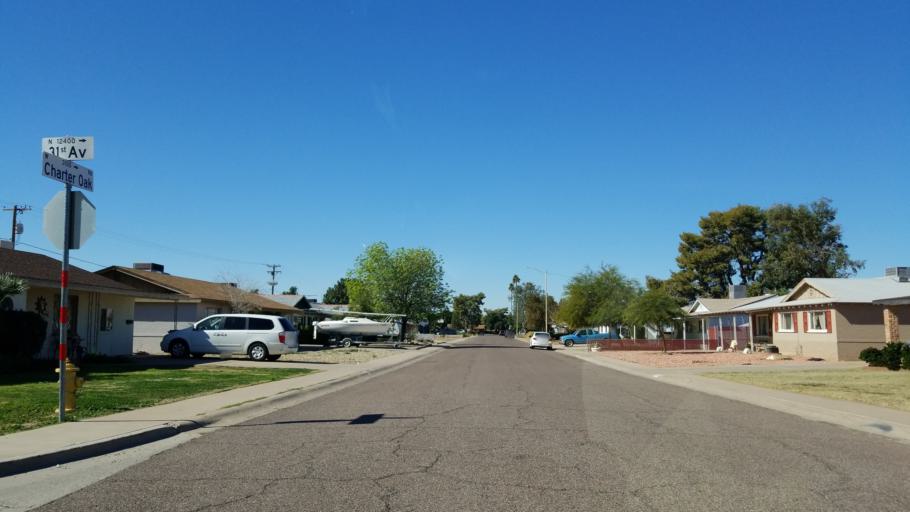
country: US
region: Arizona
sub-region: Maricopa County
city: Glendale
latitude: 33.5979
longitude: -112.1254
